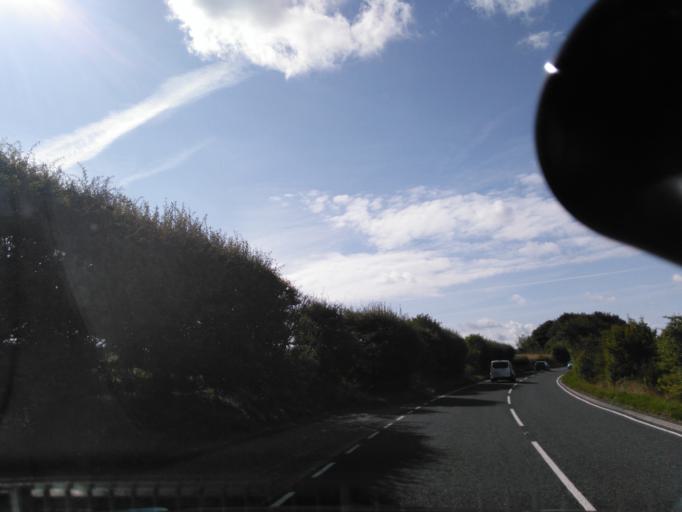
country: GB
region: England
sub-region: Wiltshire
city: Bishopstrow
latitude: 51.1462
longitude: -2.1607
